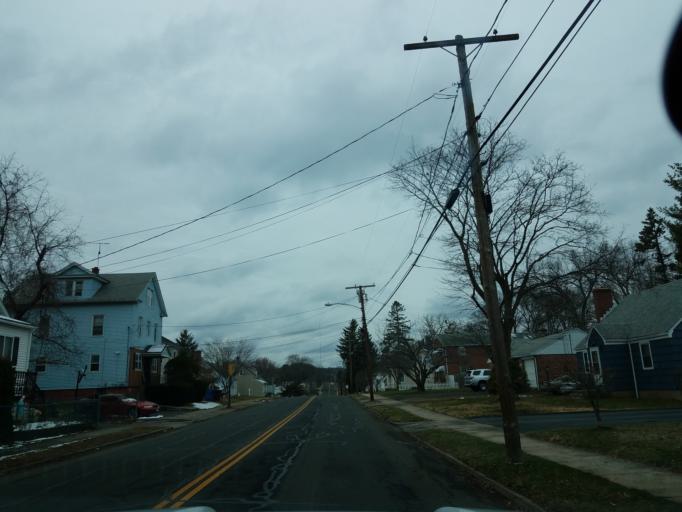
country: US
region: Connecticut
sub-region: Hartford County
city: New Britain
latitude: 41.6882
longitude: -72.7927
